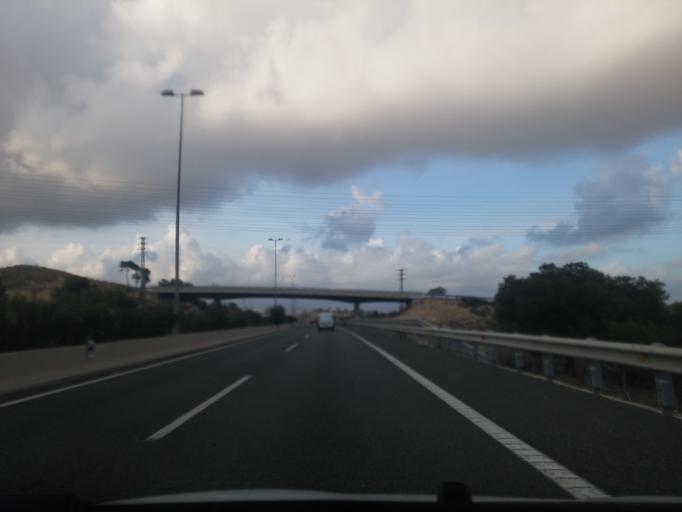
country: ES
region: Valencia
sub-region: Provincia de Alicante
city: San Juan de Alicante
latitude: 38.3916
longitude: -0.4520
